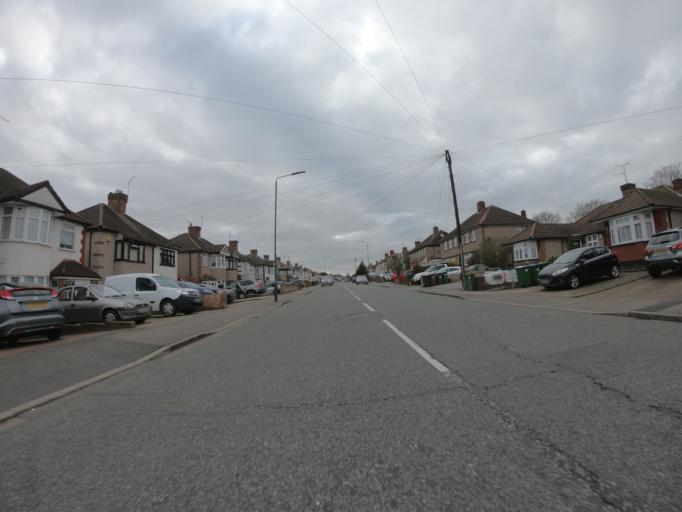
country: GB
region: England
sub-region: Greater London
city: Belvedere
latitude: 51.4786
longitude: 0.1539
